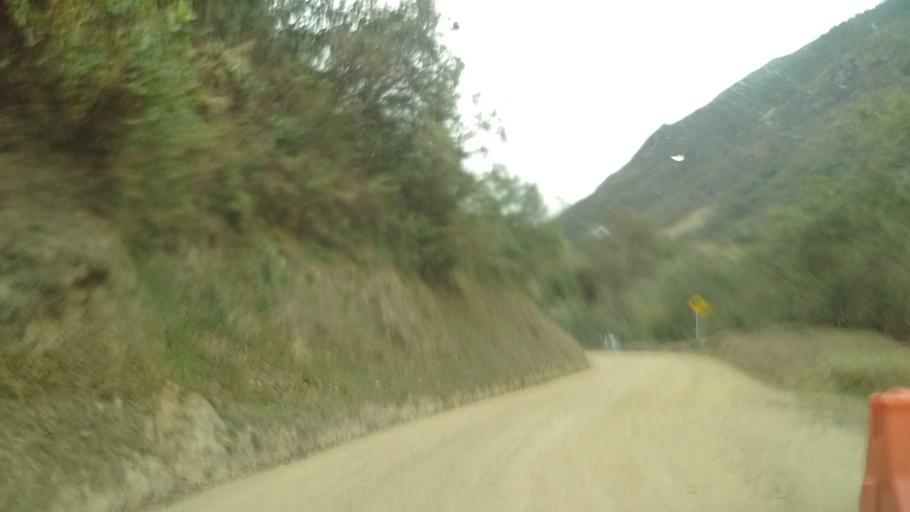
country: CO
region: Cauca
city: La Vega
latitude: 2.0153
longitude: -76.7945
